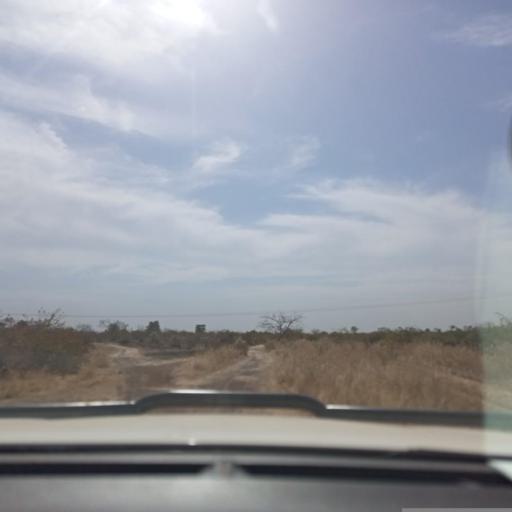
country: ML
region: Koulikoro
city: Kati
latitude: 12.7366
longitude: -8.2509
